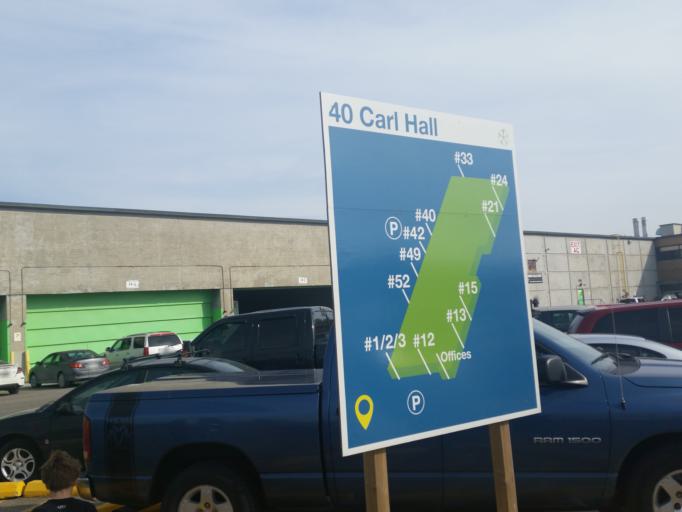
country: CA
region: Ontario
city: Concord
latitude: 43.7474
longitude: -79.4794
